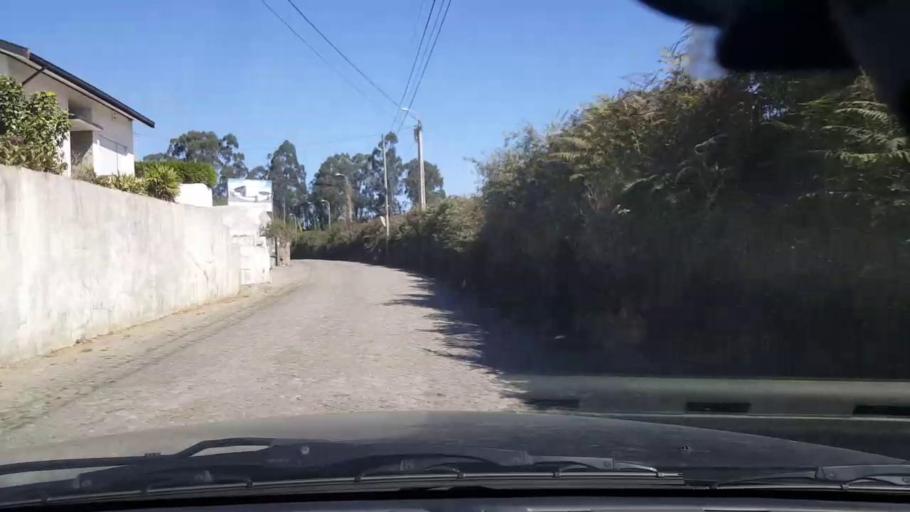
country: PT
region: Porto
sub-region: Maia
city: Gemunde
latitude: 41.2819
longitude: -8.6723
